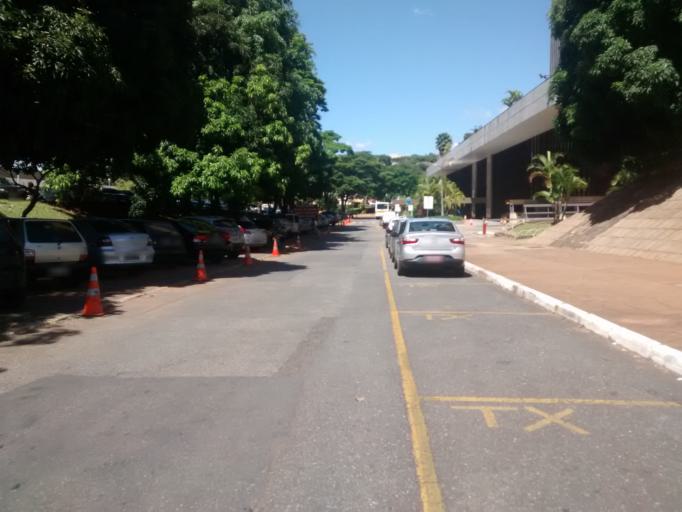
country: BR
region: Federal District
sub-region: Brasilia
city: Brasilia
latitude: -15.8027
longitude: -47.8845
